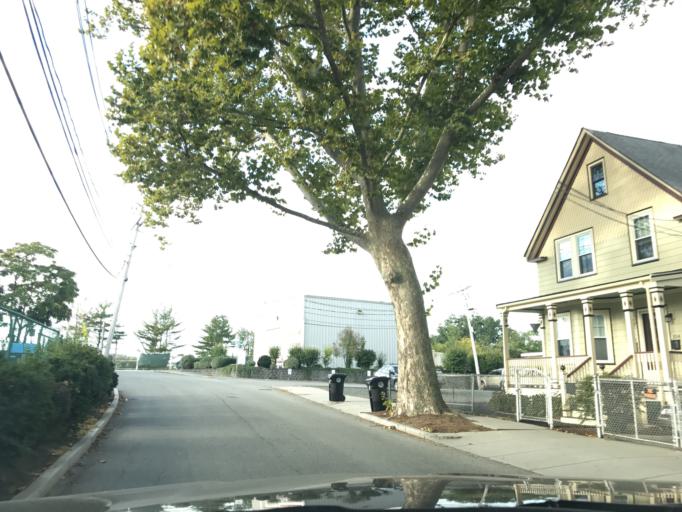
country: US
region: Massachusetts
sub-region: Middlesex County
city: Watertown
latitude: 42.3664
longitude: -71.1559
